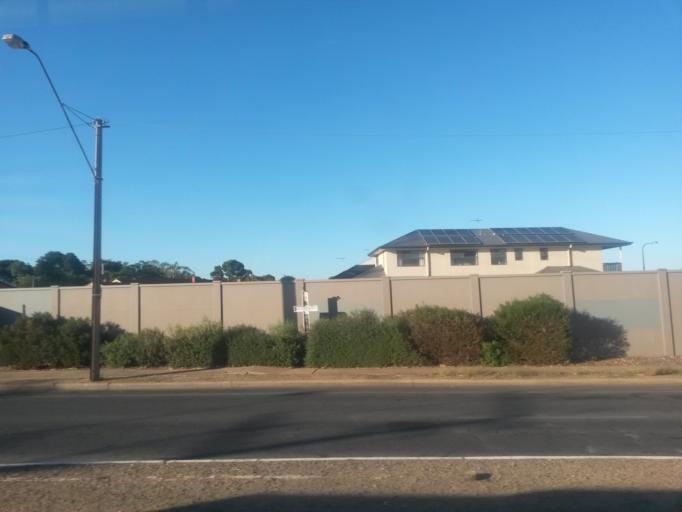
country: AU
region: South Australia
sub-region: Charles Sturt
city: Woodville North
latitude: -34.8703
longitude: 138.5403
